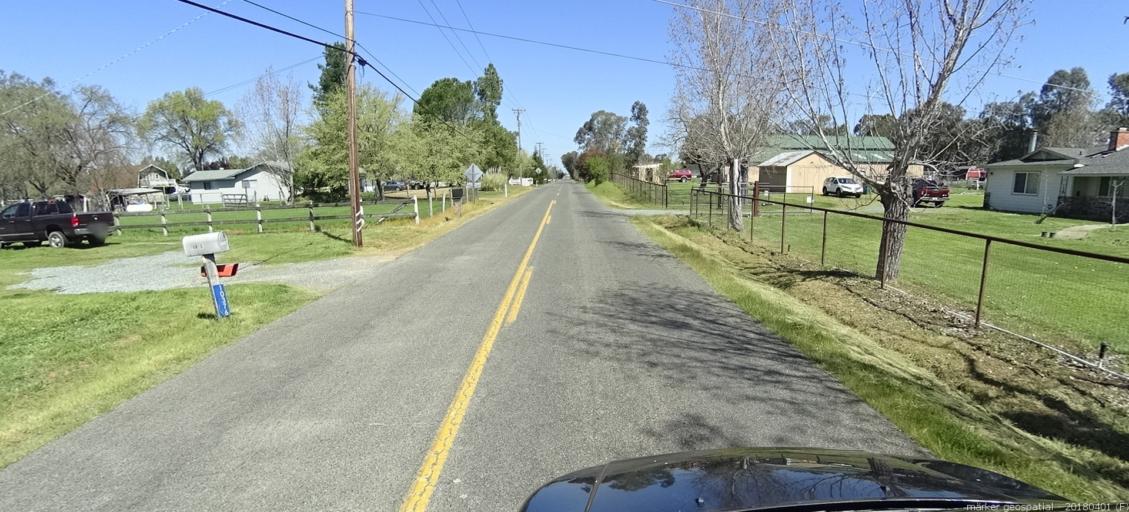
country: US
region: California
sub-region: Sacramento County
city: Wilton
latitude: 38.3807
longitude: -121.2422
